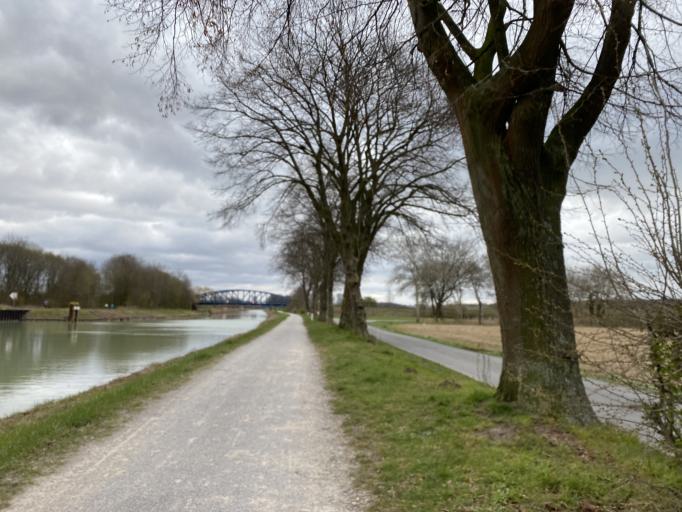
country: DE
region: North Rhine-Westphalia
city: Ahlen
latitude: 51.6906
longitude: 7.9087
